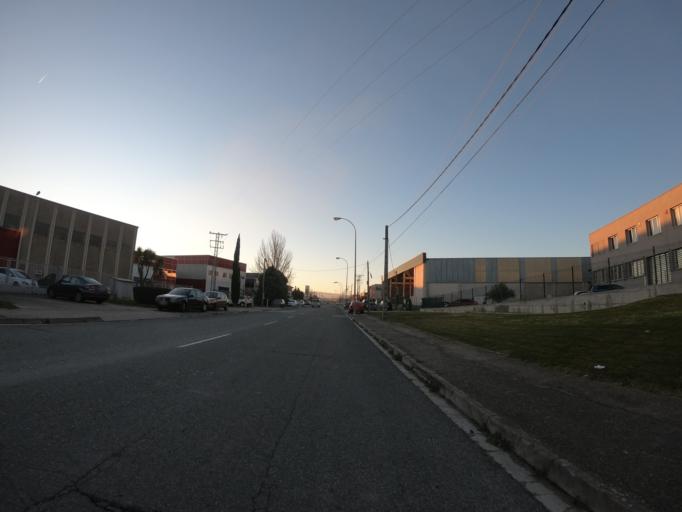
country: ES
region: Basque Country
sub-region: Provincia de Alava
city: Oyon
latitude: 42.4830
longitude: -2.4203
